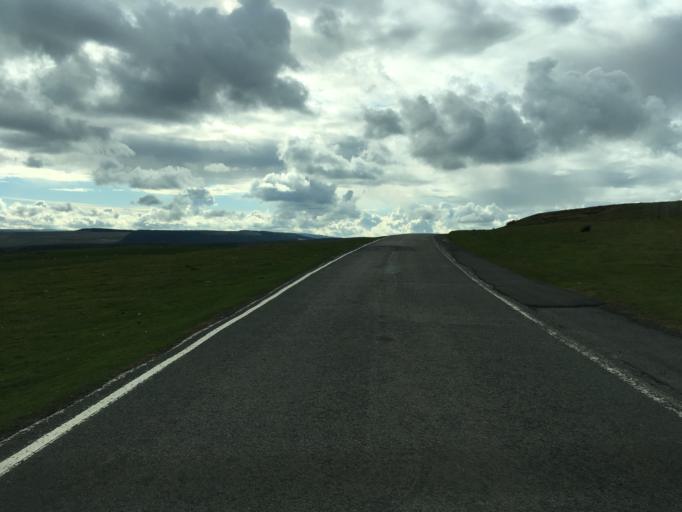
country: GB
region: Wales
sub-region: Caerphilly County Borough
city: Rhymney
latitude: 51.7191
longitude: -3.2984
